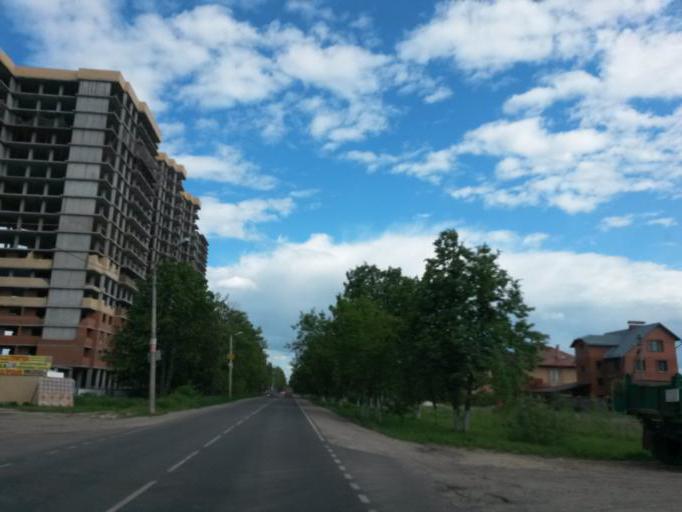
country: RU
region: Moskovskaya
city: Klimovsk
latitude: 55.3536
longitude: 37.5383
